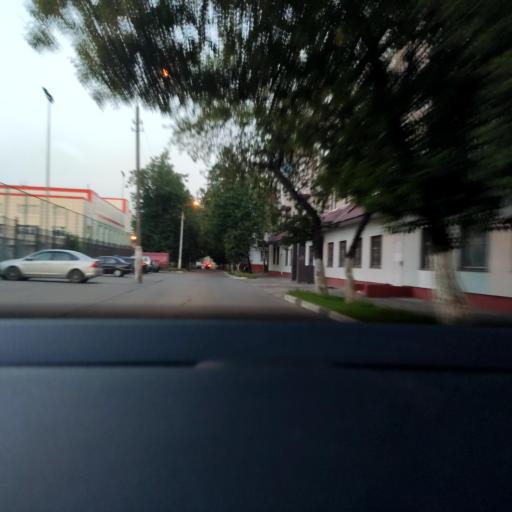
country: RU
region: Moskovskaya
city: Zheleznodorozhnyy
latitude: 55.7462
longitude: 38.0174
